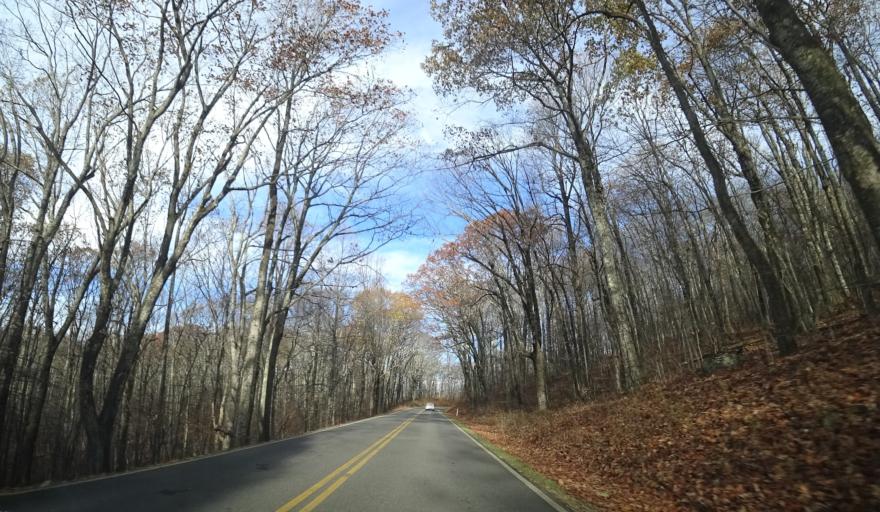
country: US
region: Virginia
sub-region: Rockingham County
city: Elkton
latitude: 38.3660
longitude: -78.5445
